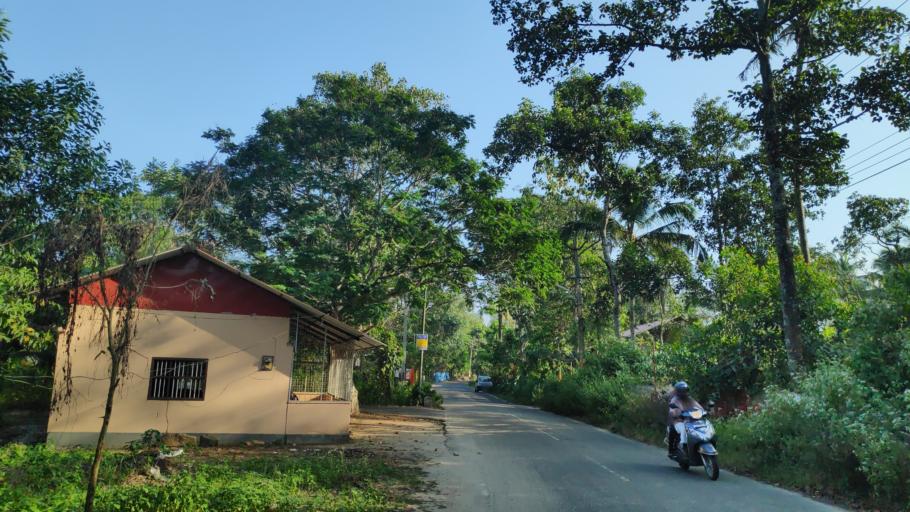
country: IN
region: Kerala
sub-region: Alappuzha
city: Alleppey
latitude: 9.5847
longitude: 76.3409
